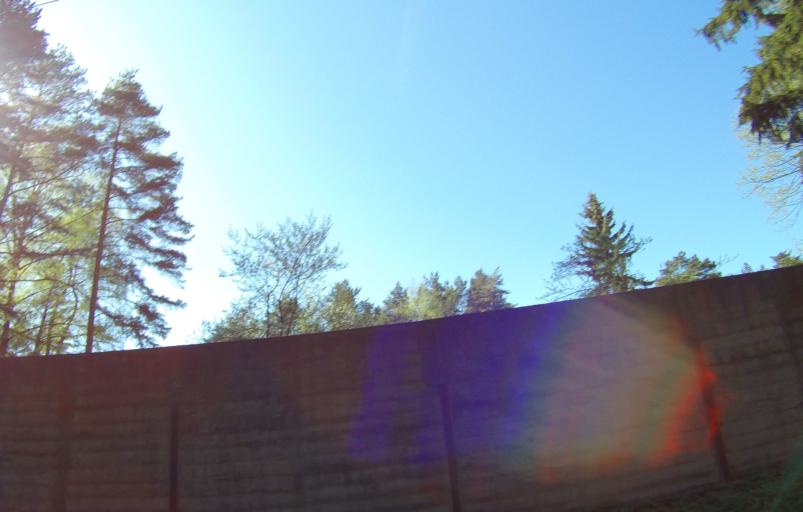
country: RU
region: Moskovskaya
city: Kratovo
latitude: 55.5887
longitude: 38.1845
